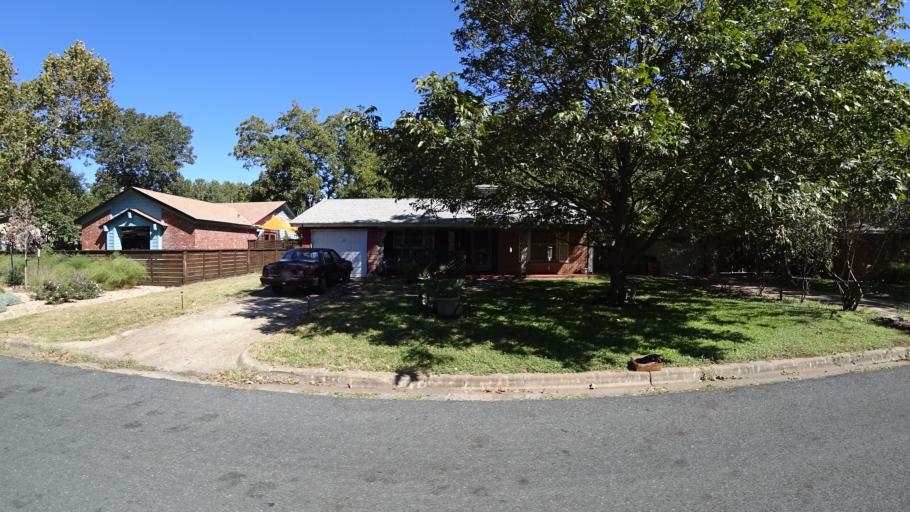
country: US
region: Texas
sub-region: Travis County
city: Rollingwood
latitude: 30.2237
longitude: -97.7878
